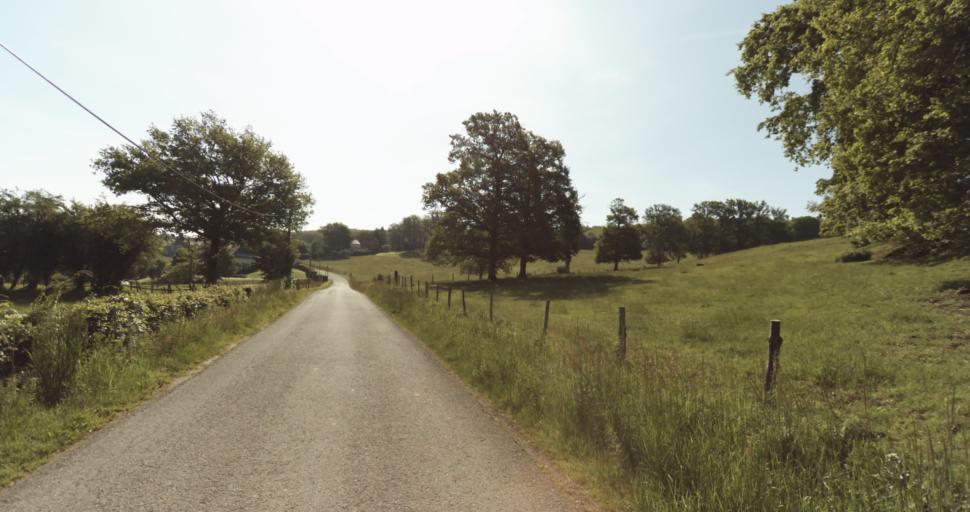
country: FR
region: Limousin
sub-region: Departement de la Haute-Vienne
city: Solignac
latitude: 45.7287
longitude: 1.2512
